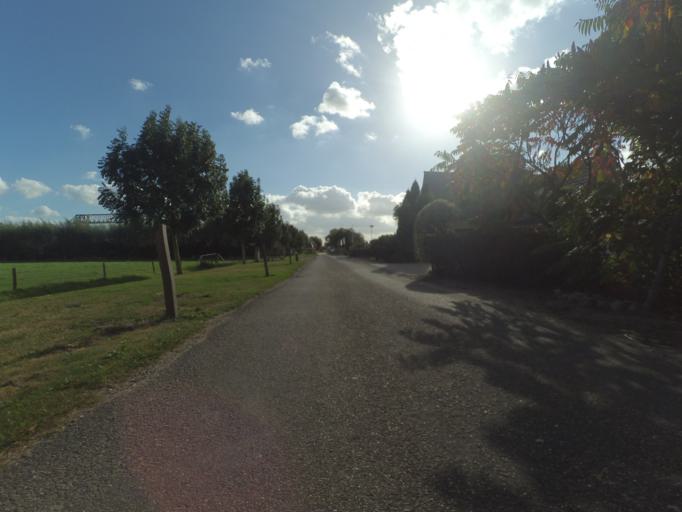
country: NL
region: Gelderland
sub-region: Gemeente Ede
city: Ederveen
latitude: 52.0758
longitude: 5.5840
